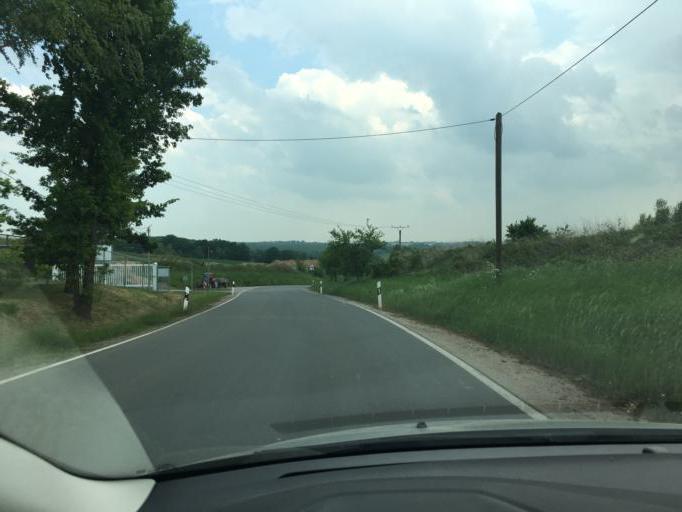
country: DE
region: Saxony
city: Rochlitz
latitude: 51.0613
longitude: 12.8040
